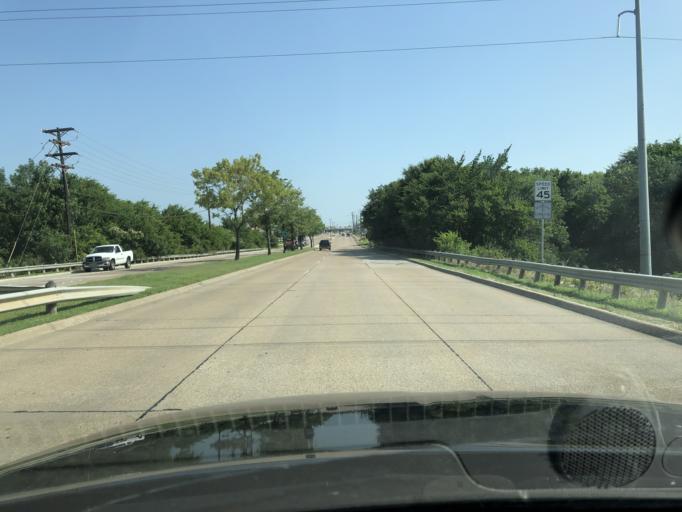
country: US
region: Texas
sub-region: Dallas County
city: Sunnyvale
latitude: 32.8337
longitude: -96.5956
